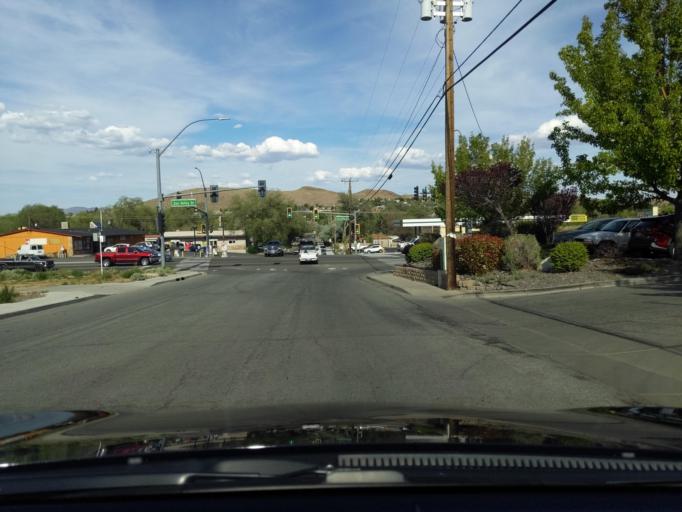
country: US
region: Nevada
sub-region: Washoe County
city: Sun Valley
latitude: 39.5819
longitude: -119.7811
